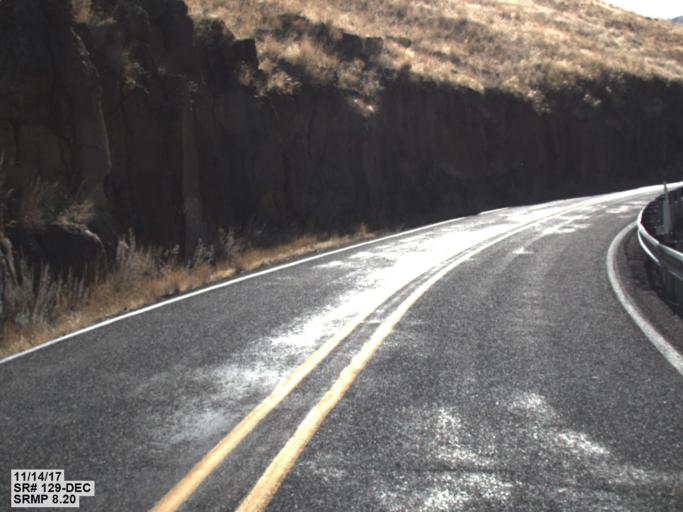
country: US
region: Washington
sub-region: Asotin County
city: Asotin
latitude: 46.0547
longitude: -117.2338
